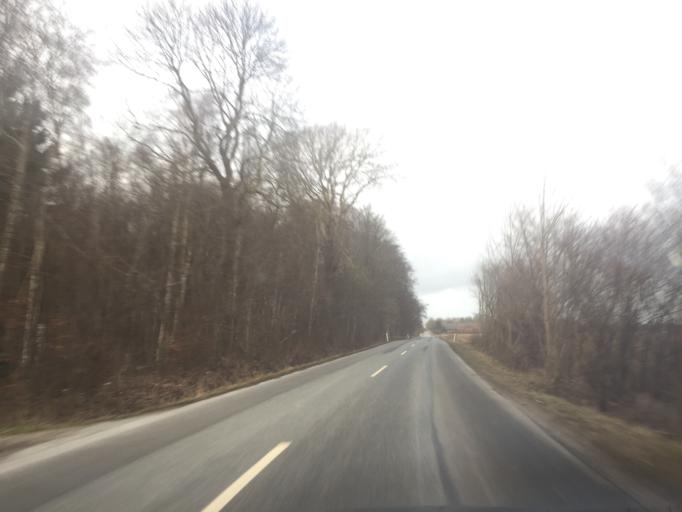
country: DK
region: Capital Region
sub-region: Egedal Kommune
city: Smorumnedre
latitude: 55.6985
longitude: 12.3230
